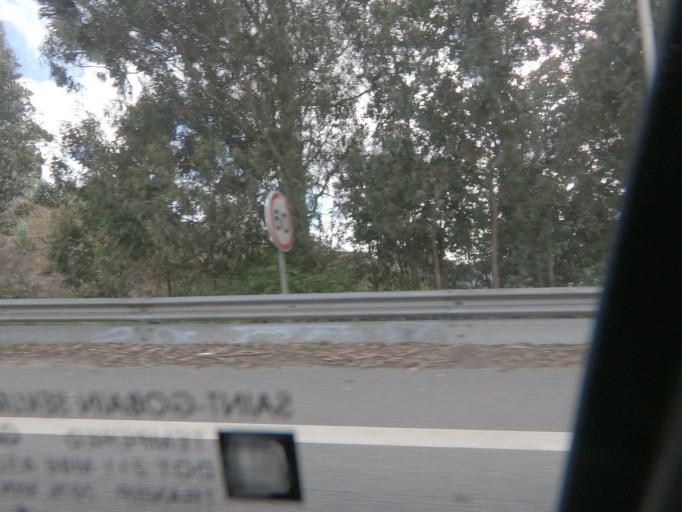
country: PT
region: Porto
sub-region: Maia
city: Pedroucos
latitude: 41.1964
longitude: -8.5913
